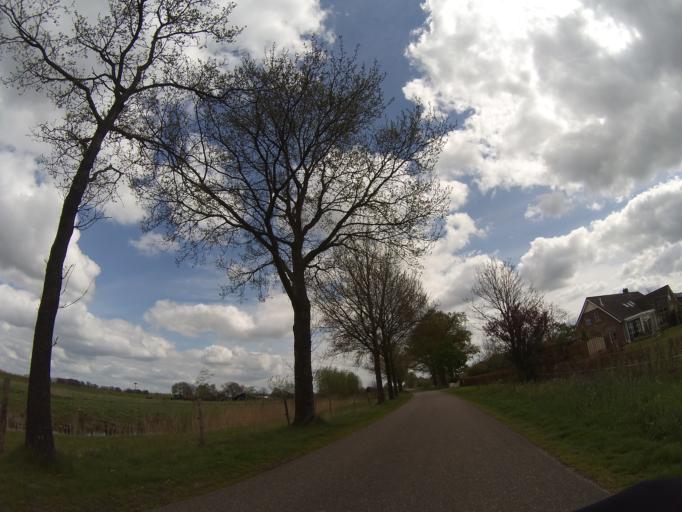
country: NL
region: Overijssel
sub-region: Gemeente Dalfsen
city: Dalfsen
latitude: 52.5157
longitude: 6.2103
